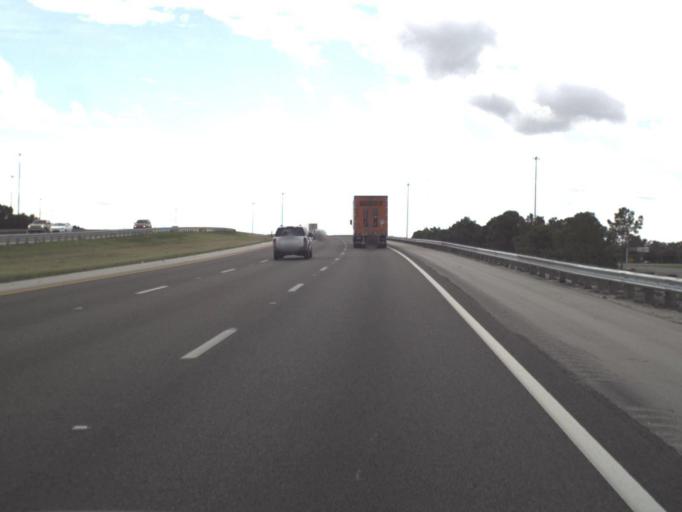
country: US
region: Florida
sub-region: Sarasota County
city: Venice Gardens
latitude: 27.1128
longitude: -82.3874
